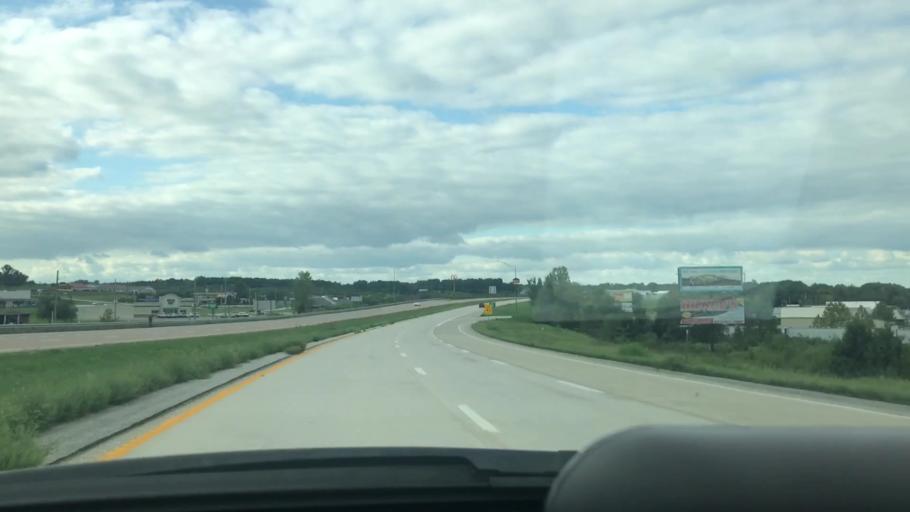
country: US
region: Missouri
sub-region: Benton County
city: Warsaw
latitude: 38.2611
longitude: -93.3660
